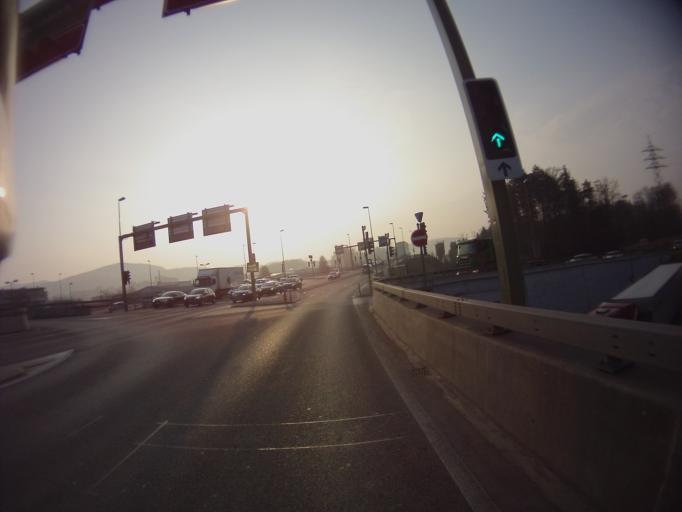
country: CH
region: Zurich
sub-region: Bezirk Affoltern
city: Obfelden / Toussen
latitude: 47.2712
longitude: 8.4387
